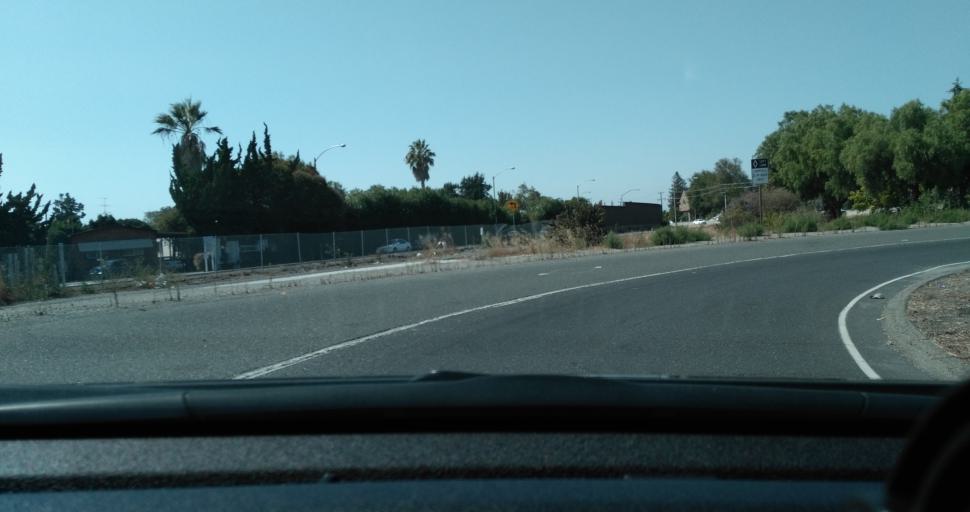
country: US
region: California
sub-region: Santa Clara County
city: Sunnyvale
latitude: 37.3949
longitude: -122.0138
